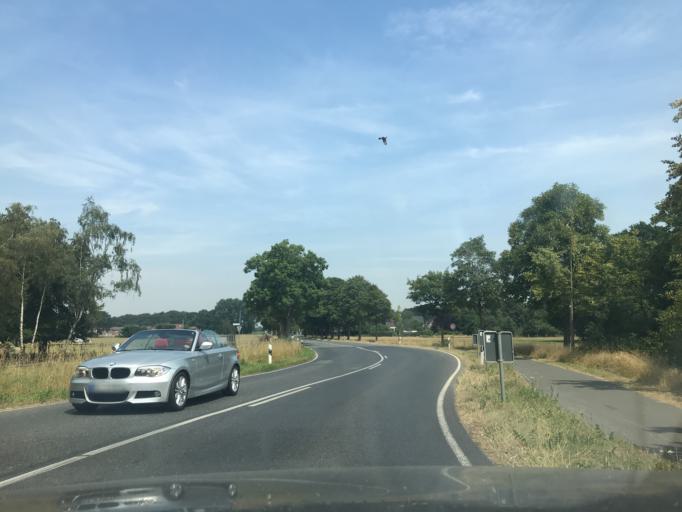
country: DE
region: North Rhine-Westphalia
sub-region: Regierungsbezirk Dusseldorf
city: Issum
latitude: 51.4949
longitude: 6.4175
